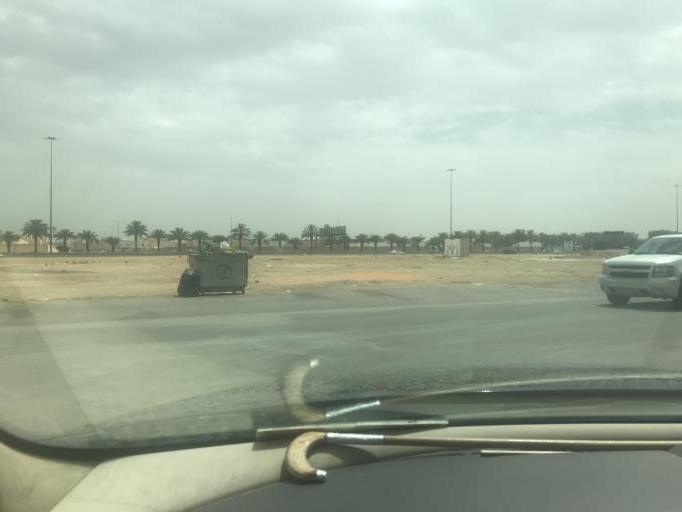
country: SA
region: Ar Riyad
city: Riyadh
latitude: 24.7916
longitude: 46.7159
